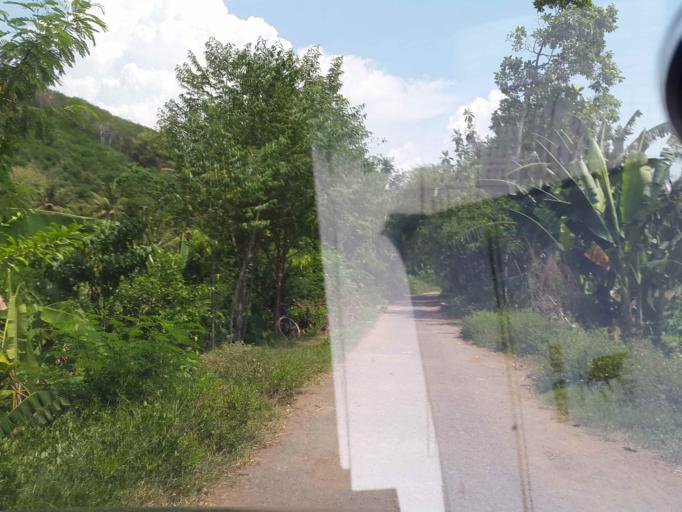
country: ID
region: West Nusa Tenggara
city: Karangkebon Timur
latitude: -8.6766
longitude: 116.0887
